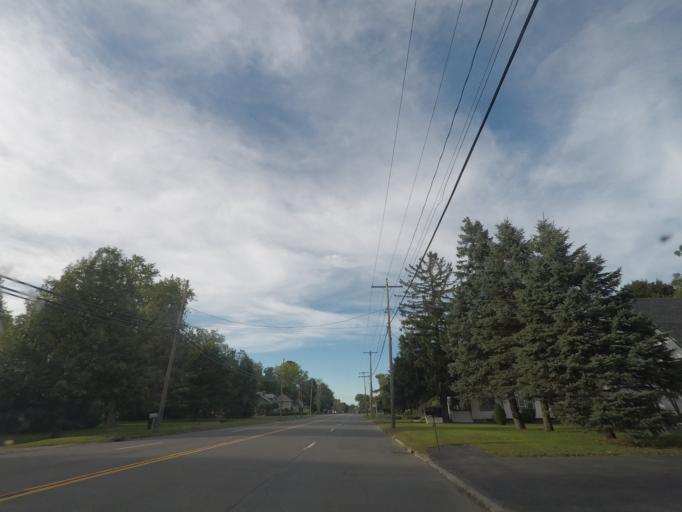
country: US
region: New York
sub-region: Rensselaer County
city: East Greenbush
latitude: 42.5749
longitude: -73.6890
